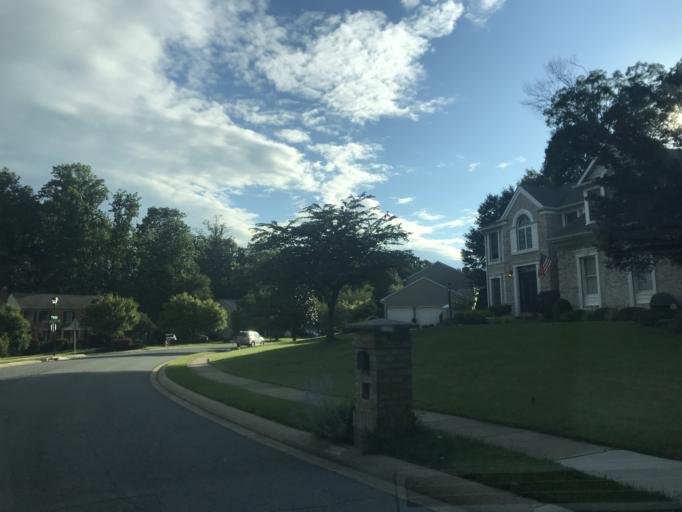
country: US
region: Maryland
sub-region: Harford County
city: South Bel Air
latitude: 39.5615
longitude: -76.3141
